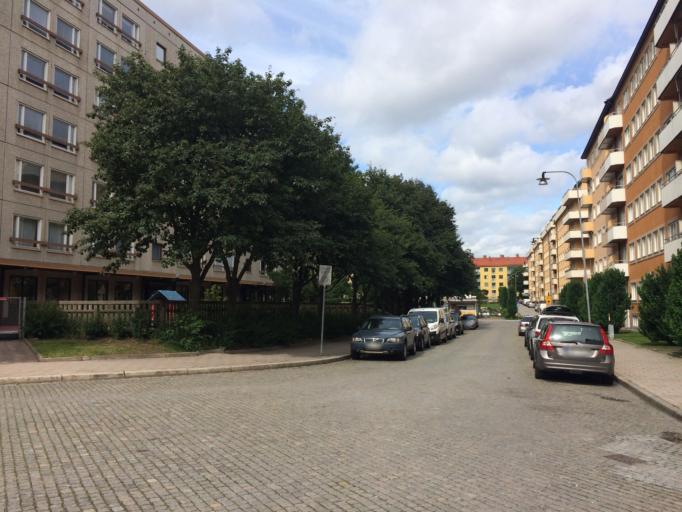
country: SE
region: Stockholm
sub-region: Stockholms Kommun
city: OEstermalm
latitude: 59.3416
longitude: 18.0892
